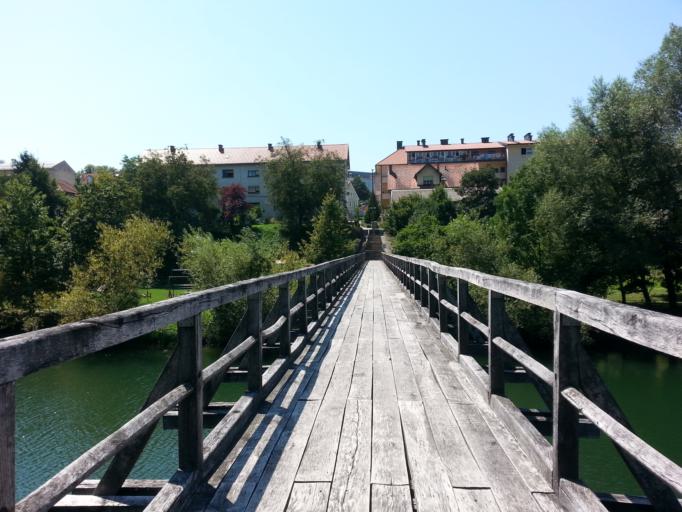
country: SI
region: Novo Mesto
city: Novo Mesto
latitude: 45.8072
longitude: 15.1668
